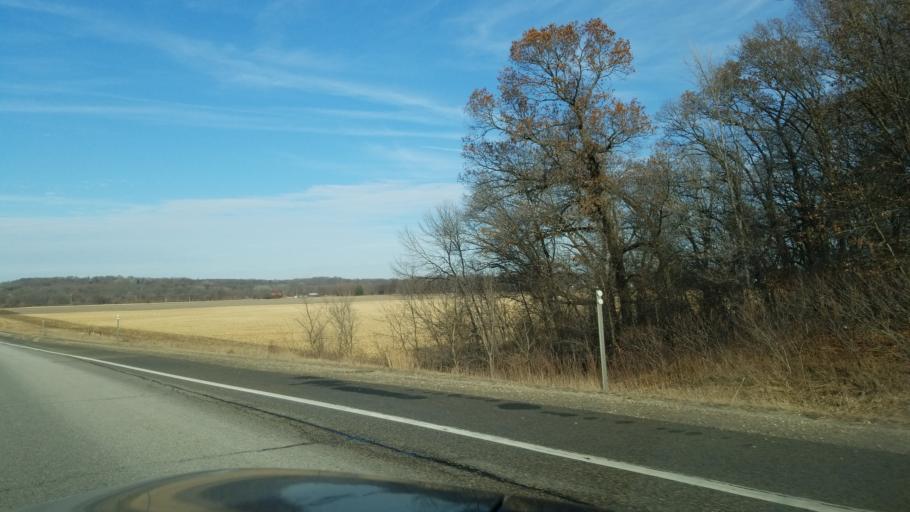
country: US
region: Iowa
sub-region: Linn County
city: Ely
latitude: 41.9306
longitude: -91.5428
